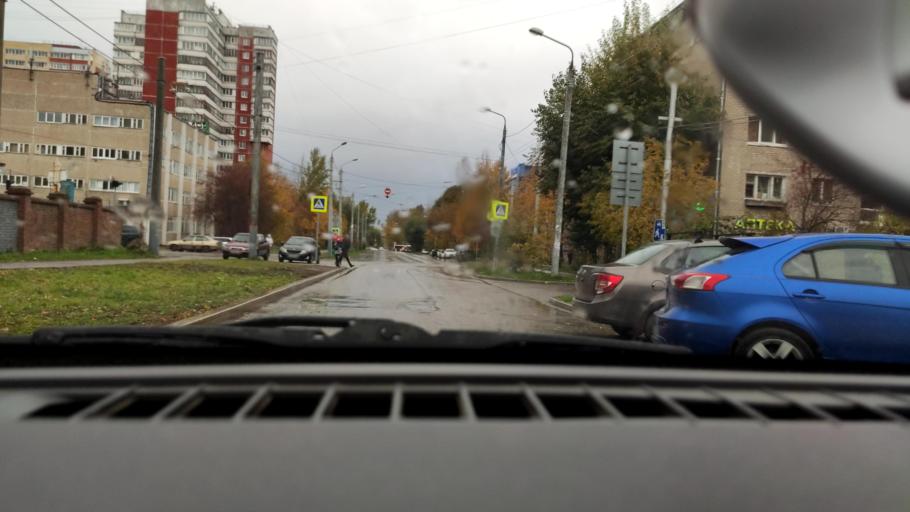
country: RU
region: Perm
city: Perm
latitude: 57.9782
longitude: 56.1958
